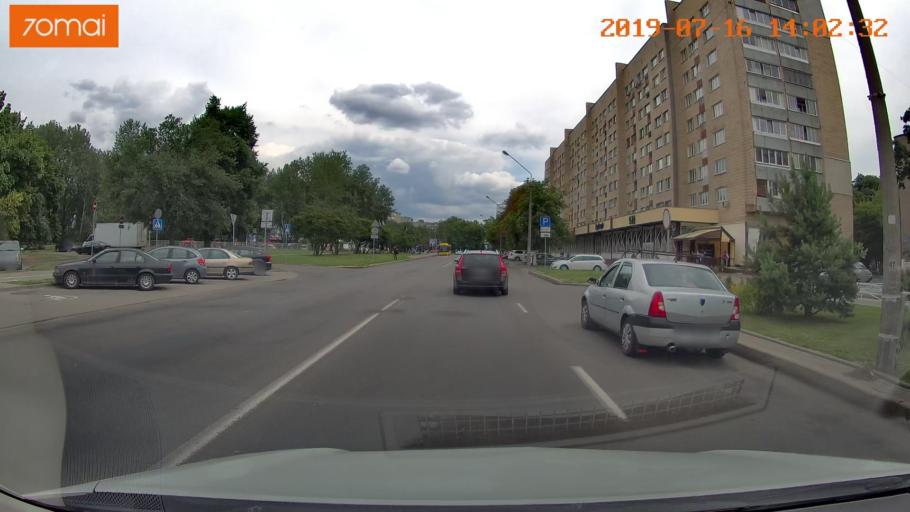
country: BY
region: Minsk
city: Minsk
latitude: 53.9271
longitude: 27.5691
